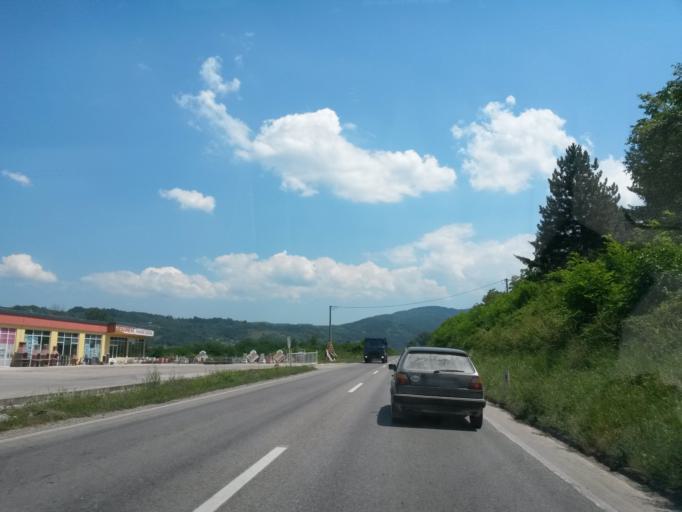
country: BA
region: Republika Srpska
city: Doboj
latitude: 44.7568
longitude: 18.0562
